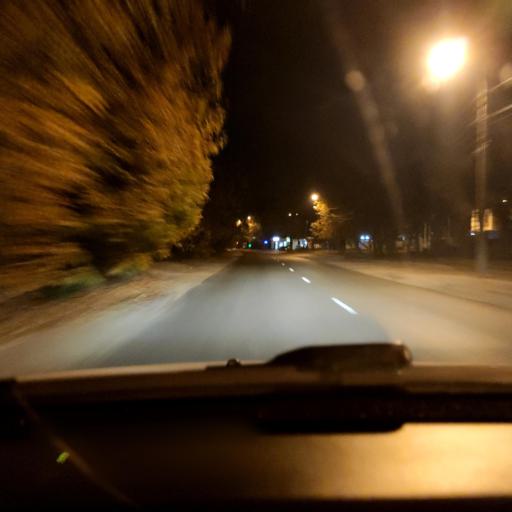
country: RU
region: Voronezj
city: Voronezh
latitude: 51.7230
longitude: 39.2171
